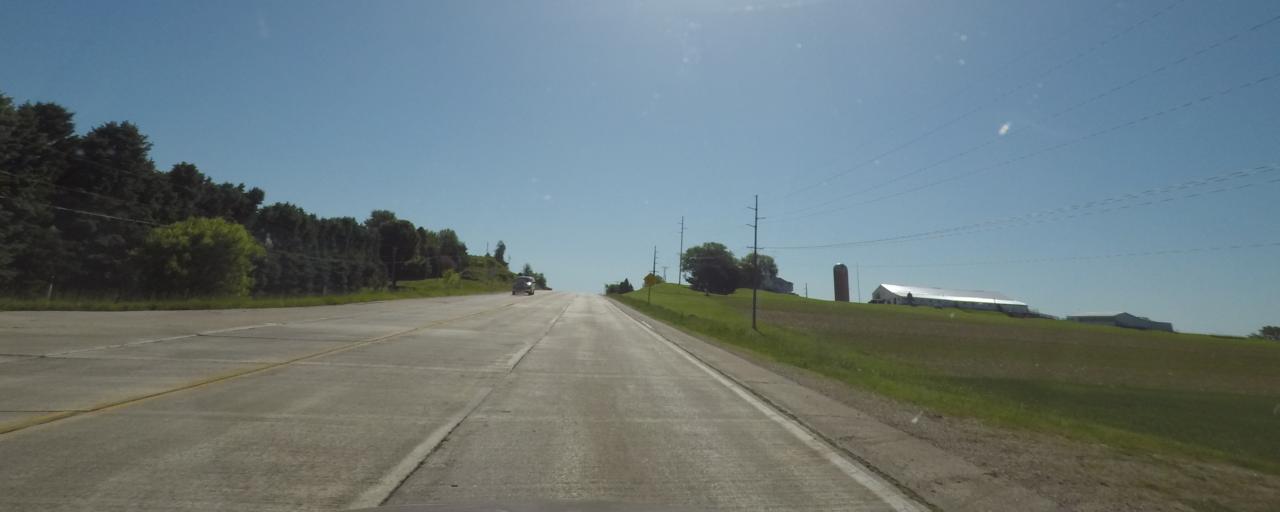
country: US
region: Wisconsin
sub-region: Fond du Lac County
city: Saint Peter
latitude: 43.7835
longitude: -88.3714
